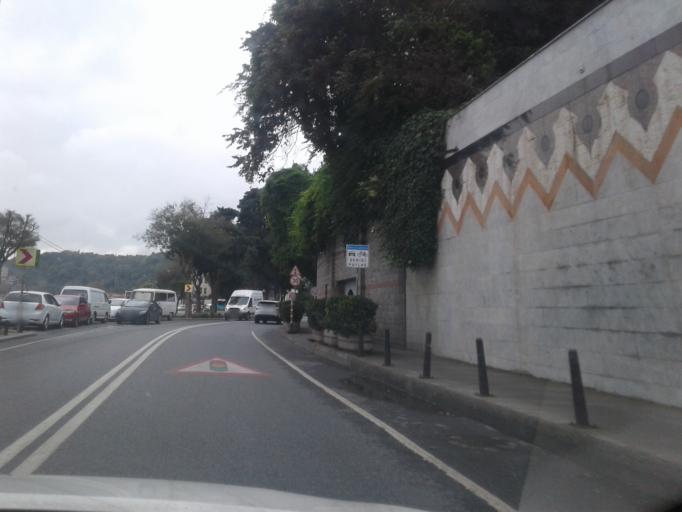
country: TR
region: Istanbul
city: Sisli
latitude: 41.1026
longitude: 29.0556
